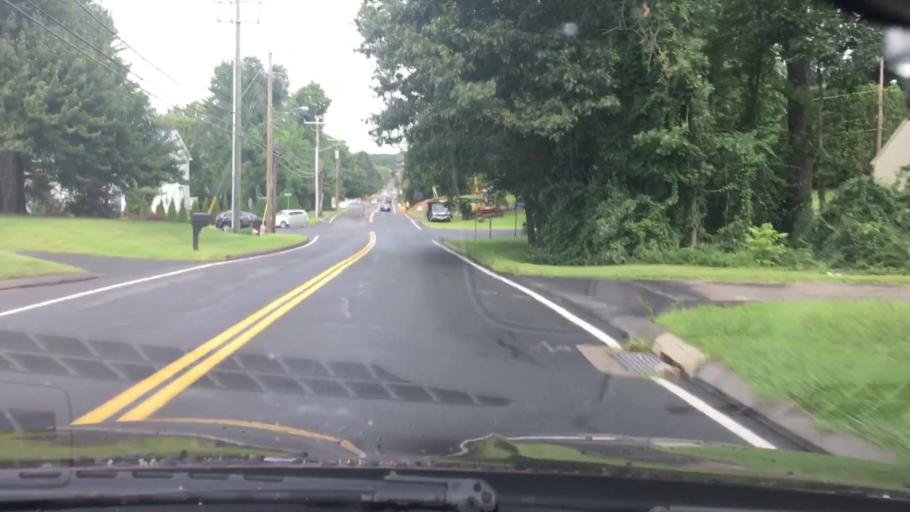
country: US
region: Connecticut
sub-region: Hartford County
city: Manchester
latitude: 41.7505
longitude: -72.5399
